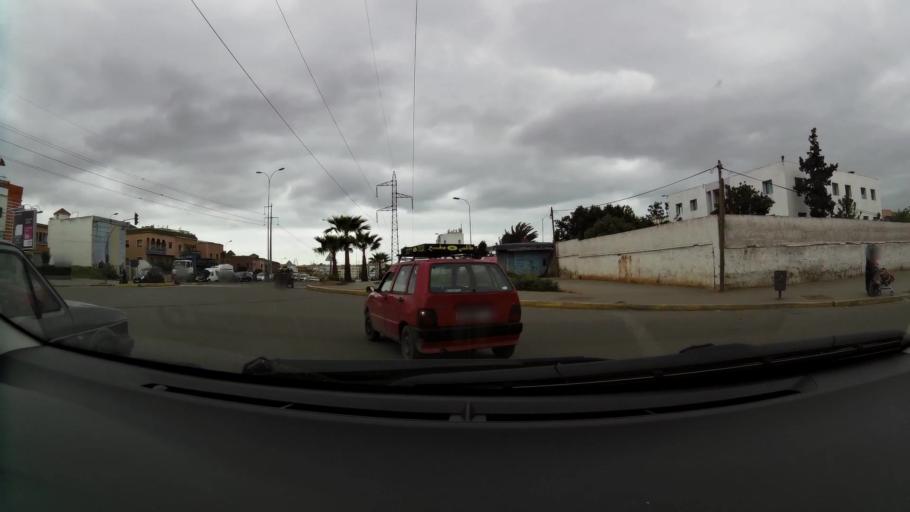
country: MA
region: Grand Casablanca
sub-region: Mediouna
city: Tit Mellil
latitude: 33.5655
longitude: -7.5291
